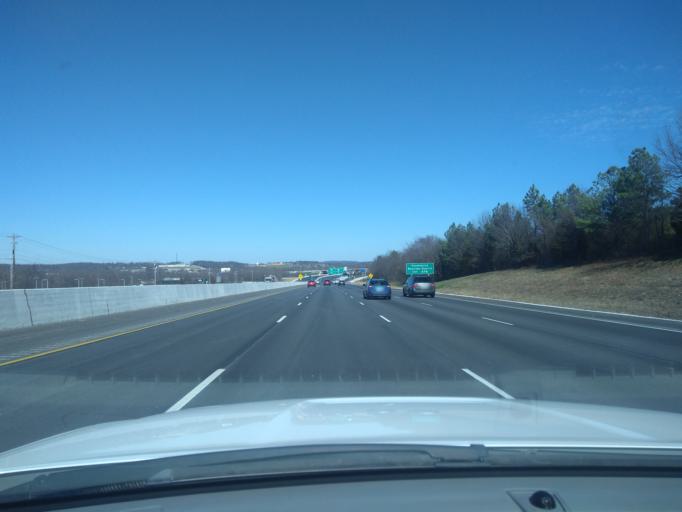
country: US
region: Arkansas
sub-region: Washington County
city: Johnson
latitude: 36.0996
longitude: -94.1852
